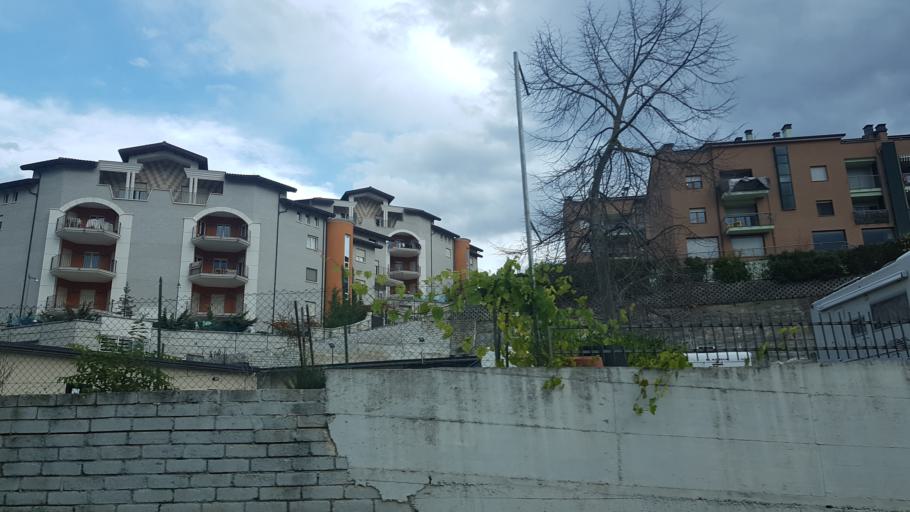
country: IT
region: Abruzzo
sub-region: Provincia dell' Aquila
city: L'Aquila
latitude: 42.3471
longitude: 13.4112
